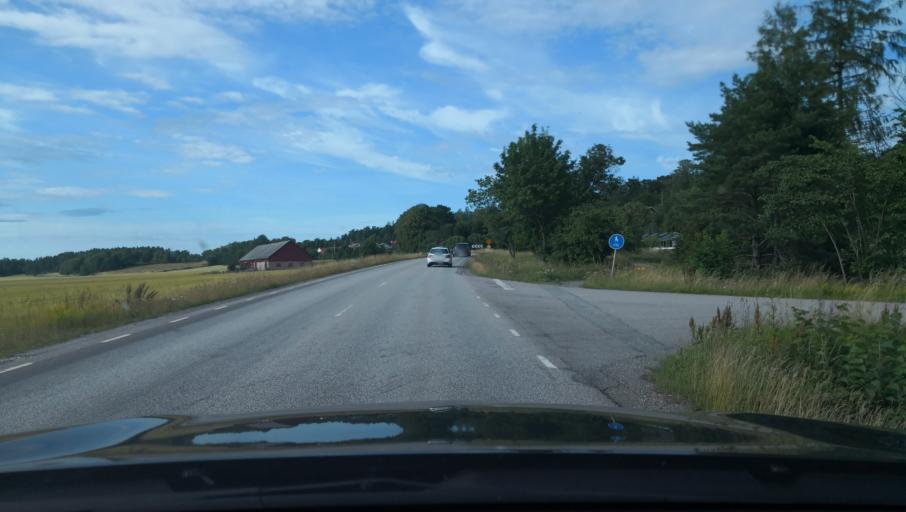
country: SE
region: Uppsala
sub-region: Habo Kommun
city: Balsta
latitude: 59.5923
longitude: 17.5104
